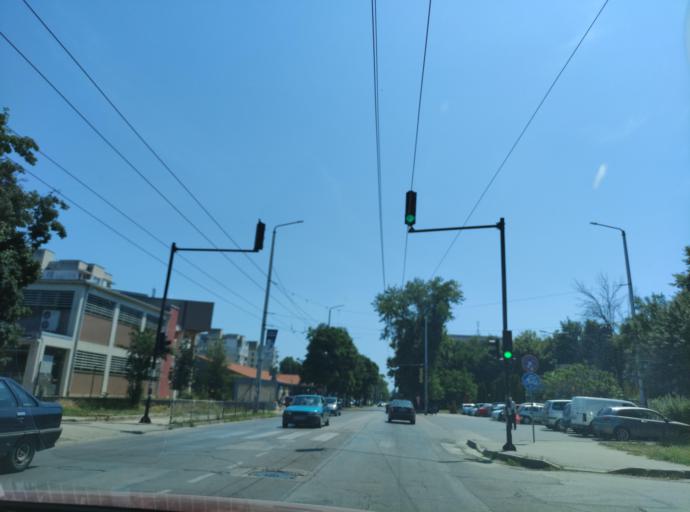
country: BG
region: Pleven
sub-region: Obshtina Pleven
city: Pleven
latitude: 43.4240
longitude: 24.5939
